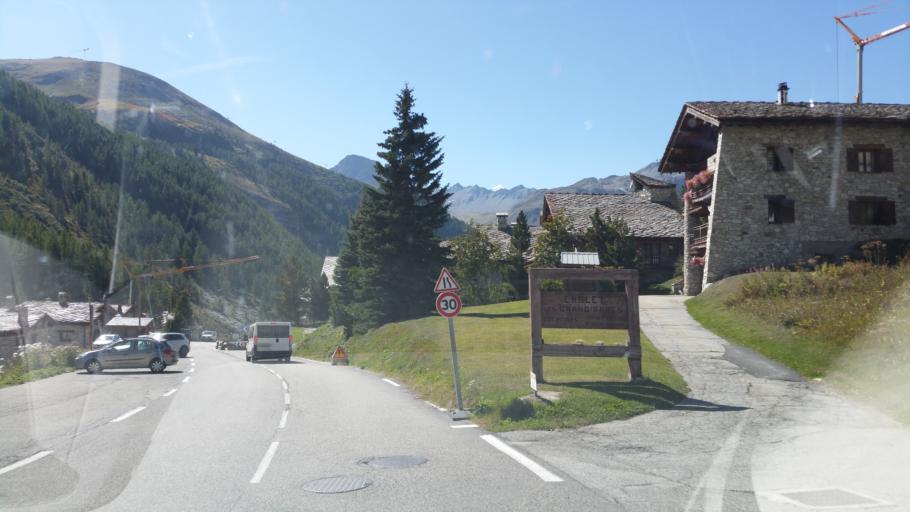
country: FR
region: Rhone-Alpes
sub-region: Departement de la Savoie
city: Val-d'Isere
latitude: 45.4504
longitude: 7.0107
